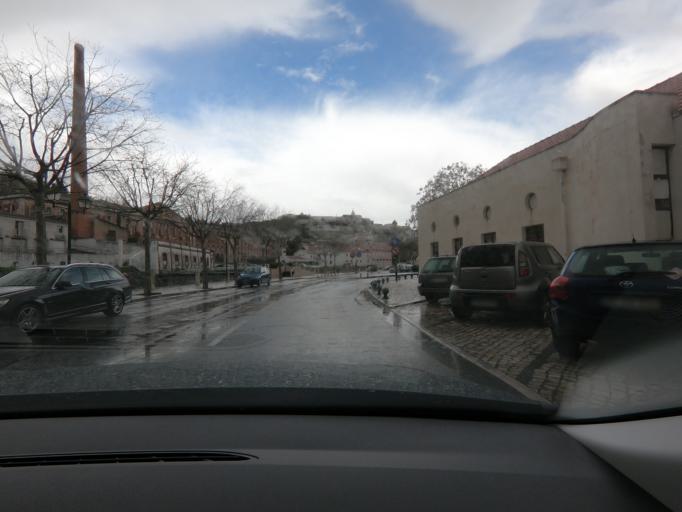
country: PT
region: Lisbon
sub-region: Alenquer
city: Alenquer
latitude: 39.0502
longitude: -9.0064
